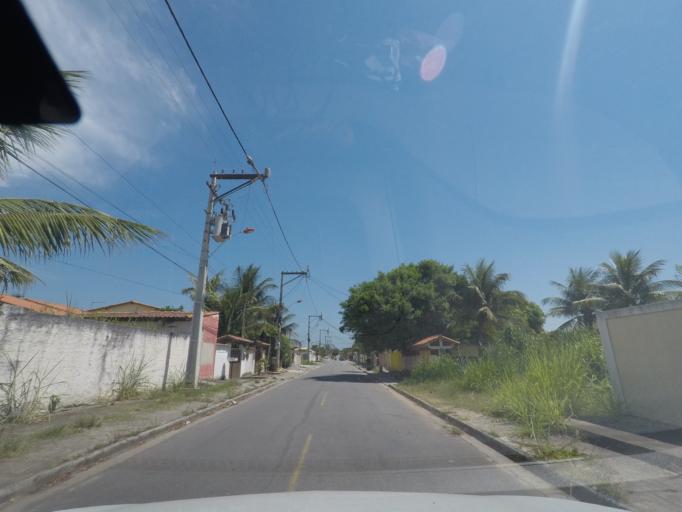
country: BR
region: Rio de Janeiro
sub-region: Marica
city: Marica
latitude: -22.9604
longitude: -42.9594
